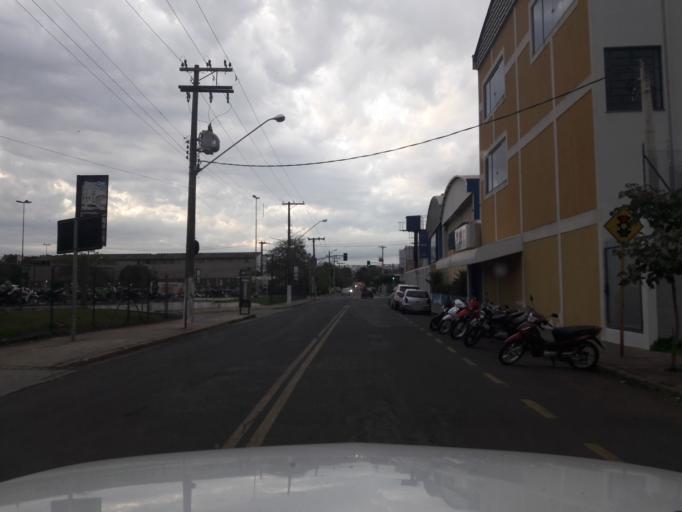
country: BR
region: Sao Paulo
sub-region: Moji-Guacu
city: Mogi-Gaucu
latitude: -22.3683
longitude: -46.9513
